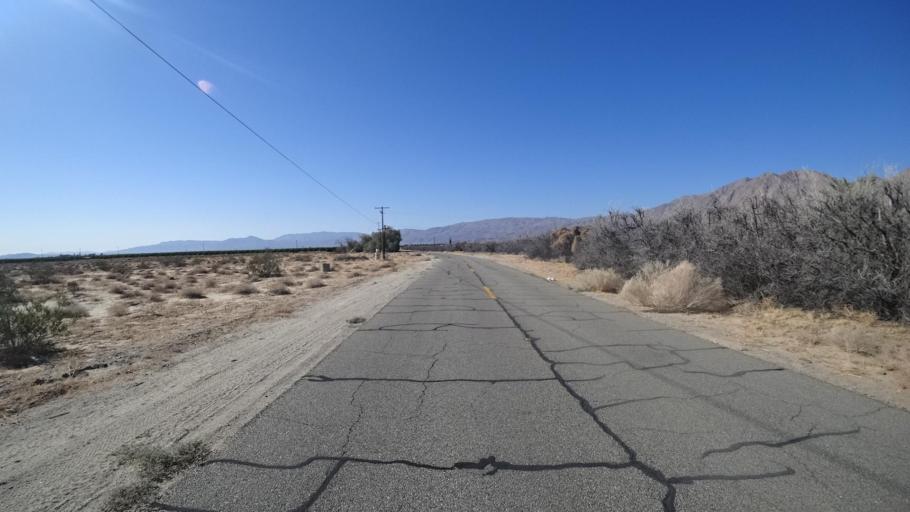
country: US
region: California
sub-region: San Diego County
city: Borrego Springs
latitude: 33.3224
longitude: -116.3677
